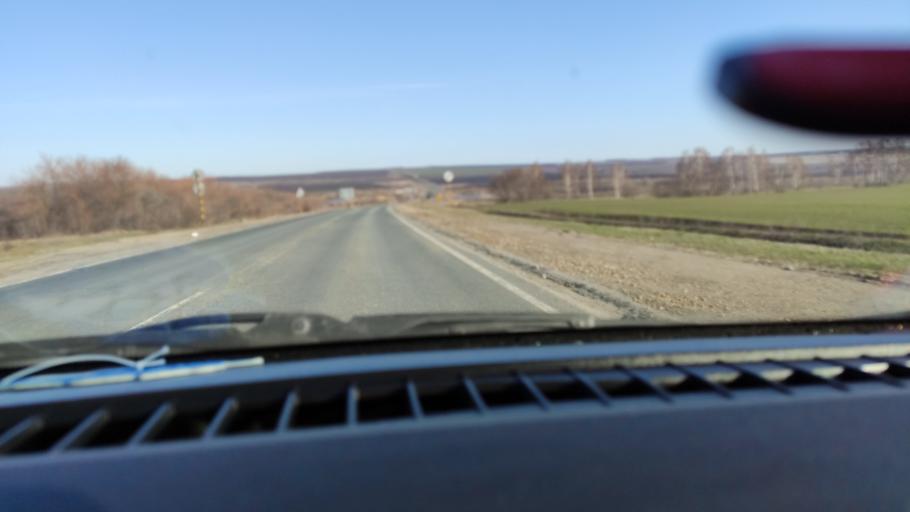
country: RU
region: Saratov
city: Dukhovnitskoye
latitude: 52.7263
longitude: 48.2605
